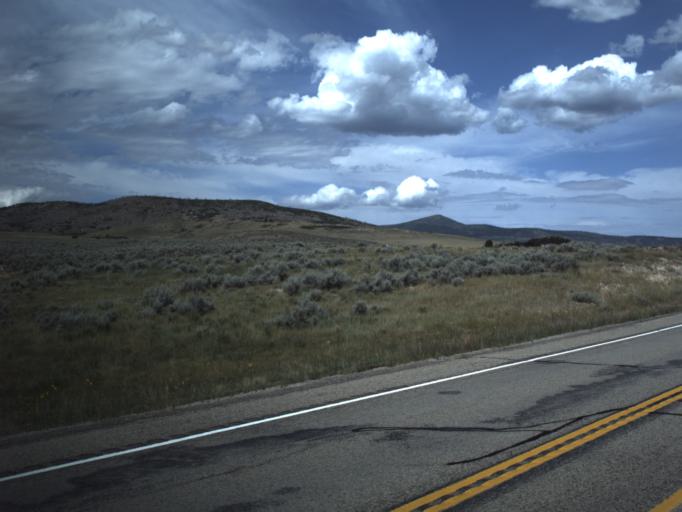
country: US
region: Utah
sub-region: Sanpete County
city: Fairview
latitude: 39.7051
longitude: -111.4687
